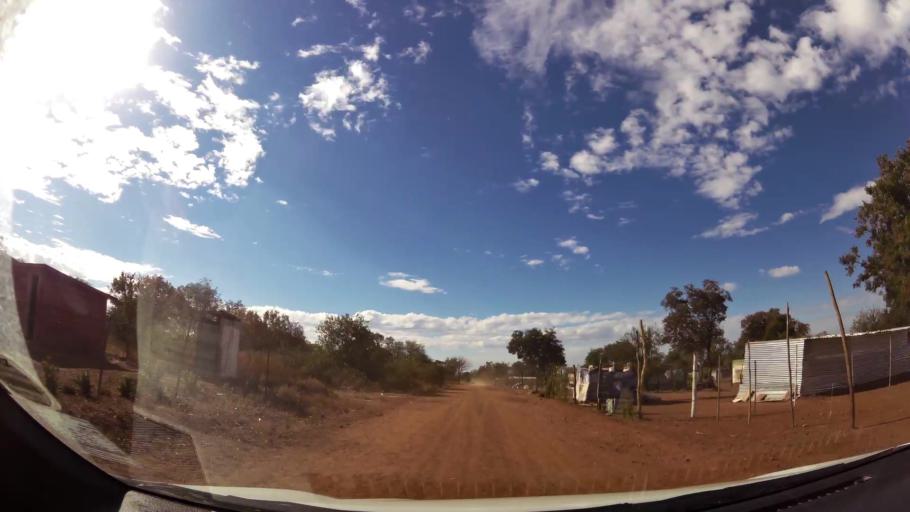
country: ZA
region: Limpopo
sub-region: Waterberg District Municipality
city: Warmbaths
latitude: -24.8752
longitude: 28.2757
